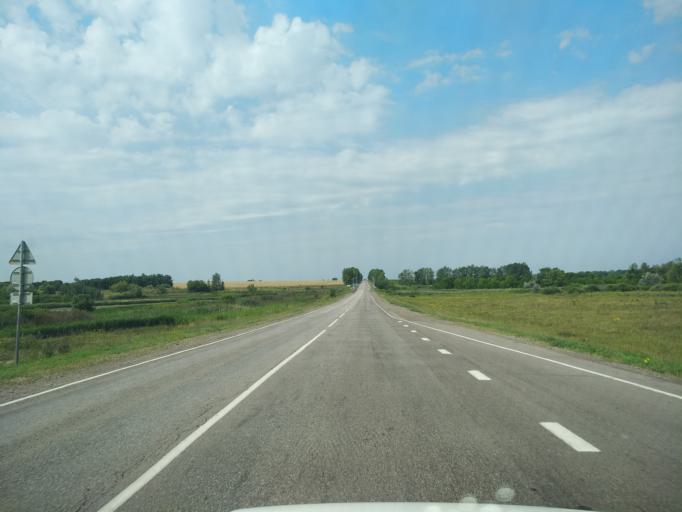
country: RU
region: Voronezj
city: Verkhnyaya Khava
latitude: 51.7013
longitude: 39.9703
